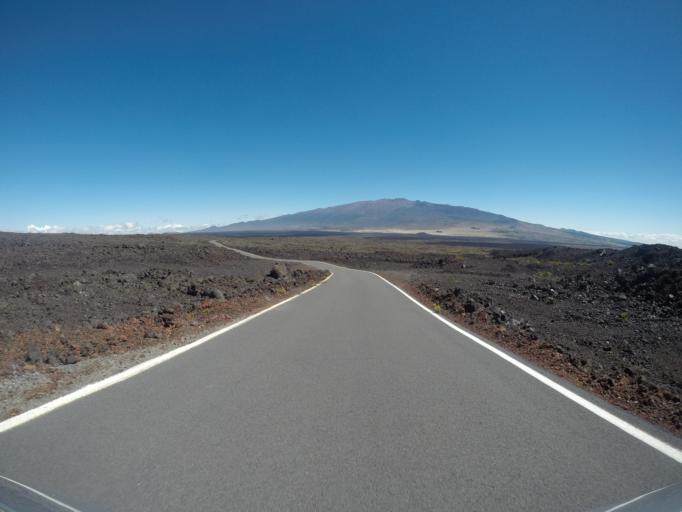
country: US
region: Hawaii
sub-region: Hawaii County
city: Volcano
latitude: 19.6194
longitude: -155.4726
